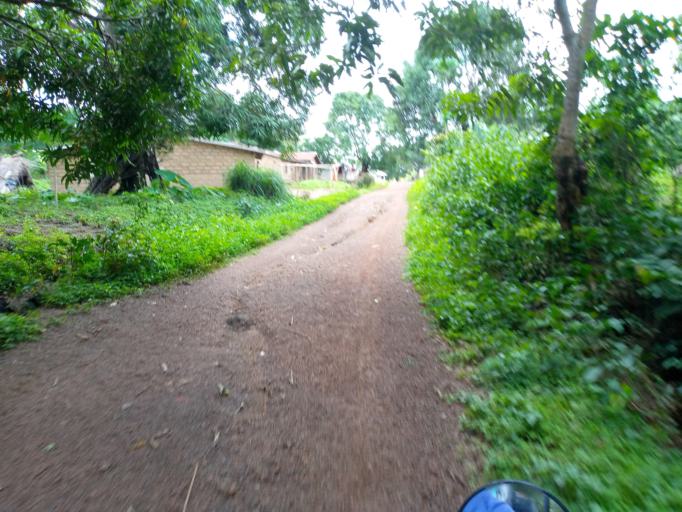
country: SL
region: Northern Province
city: Mange
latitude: 8.9733
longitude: -12.8300
